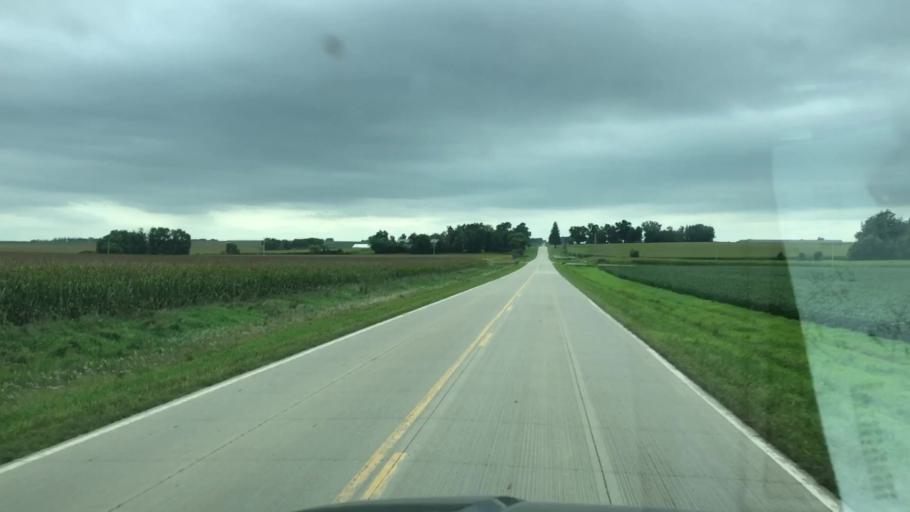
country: US
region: Iowa
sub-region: Sioux County
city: Alton
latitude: 43.1155
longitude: -95.9788
